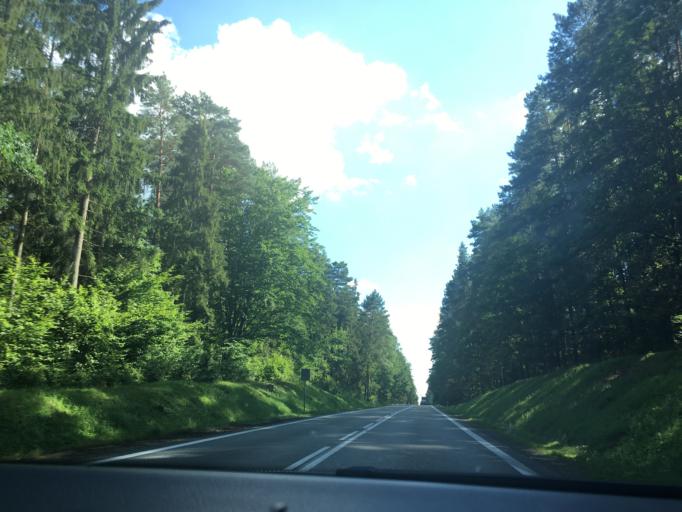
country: PL
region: Podlasie
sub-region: Powiat bialostocki
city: Wasilkow
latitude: 53.3154
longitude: 23.1276
